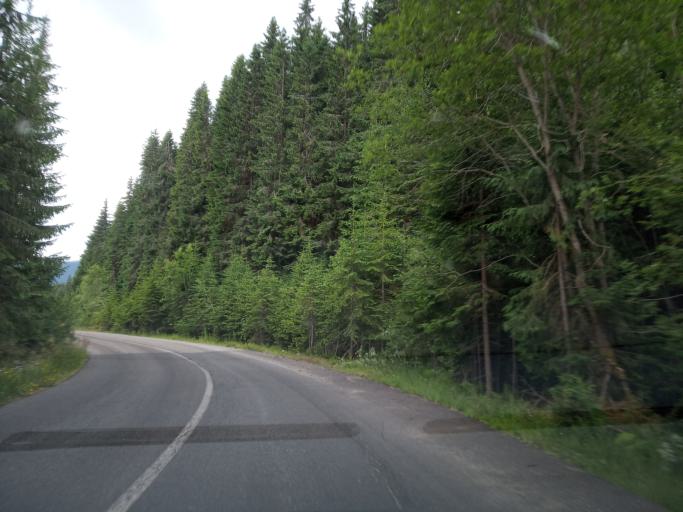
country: RO
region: Gorj
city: Novaci-Straini
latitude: 45.4257
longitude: 23.6875
